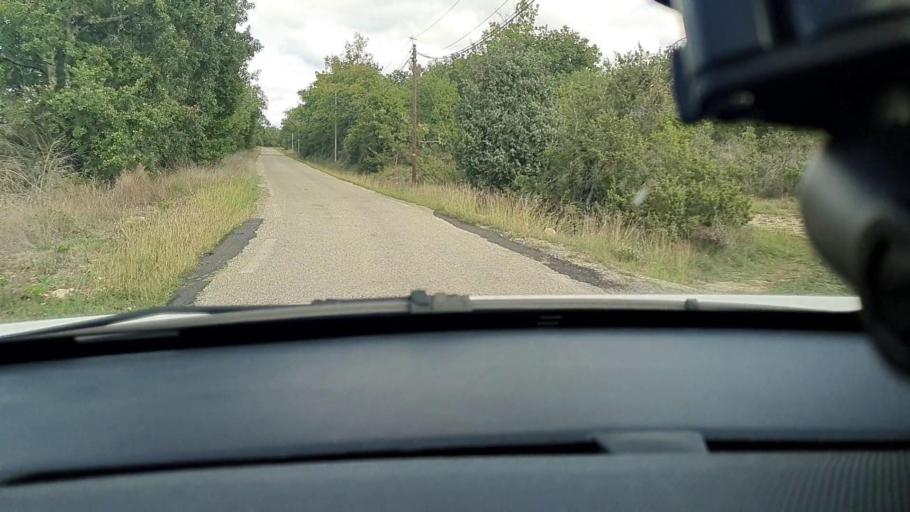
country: FR
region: Languedoc-Roussillon
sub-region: Departement du Gard
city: Mons
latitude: 44.1646
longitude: 4.2982
